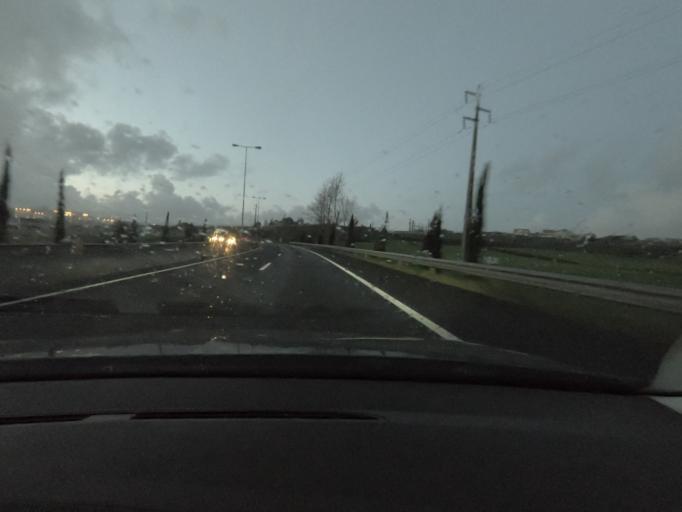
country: PT
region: Lisbon
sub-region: Oeiras
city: Porto Salvo
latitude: 38.7289
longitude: -9.2959
